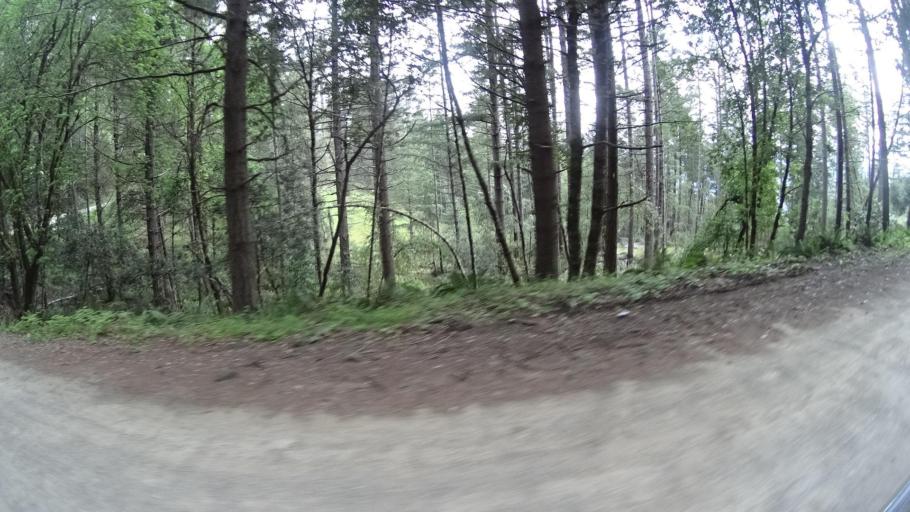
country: US
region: California
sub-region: Humboldt County
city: Redway
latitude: 40.2559
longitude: -123.7670
